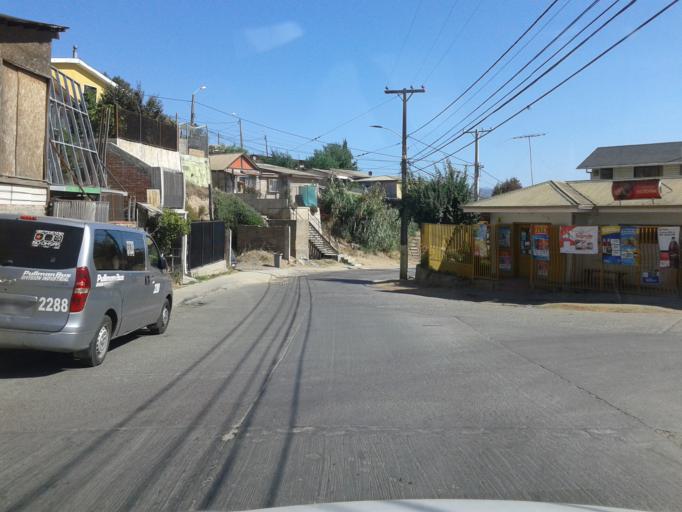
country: CL
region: Valparaiso
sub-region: Provincia de Quillota
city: Quillota
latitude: -32.8748
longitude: -71.2524
